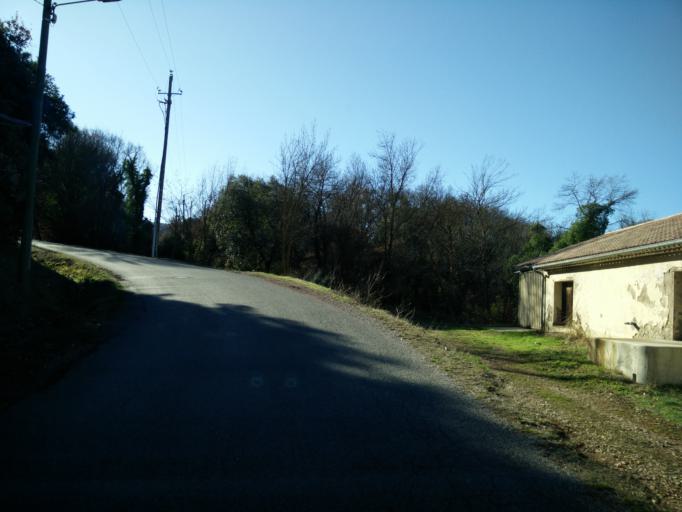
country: FR
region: Provence-Alpes-Cote d'Azur
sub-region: Departement du Var
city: Gonfaron
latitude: 43.3177
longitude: 6.2896
